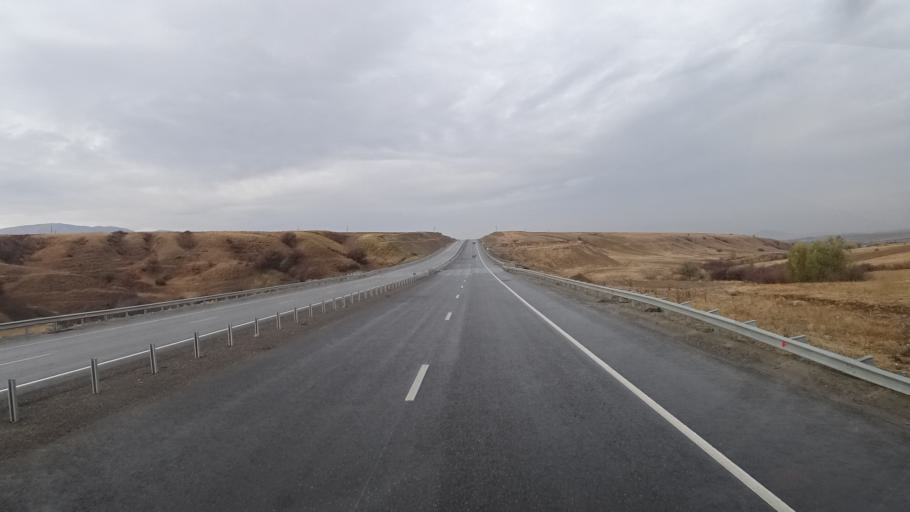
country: KZ
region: Ongtustik Qazaqstan
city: Turar Ryskulov
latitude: 42.5079
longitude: 70.4165
